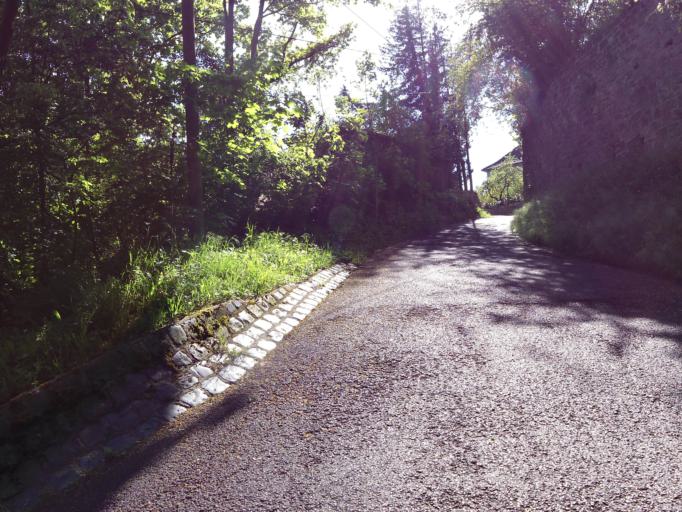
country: DE
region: Bavaria
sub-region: Regierungsbezirk Unterfranken
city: Wuerzburg
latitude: 49.8058
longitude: 9.9419
